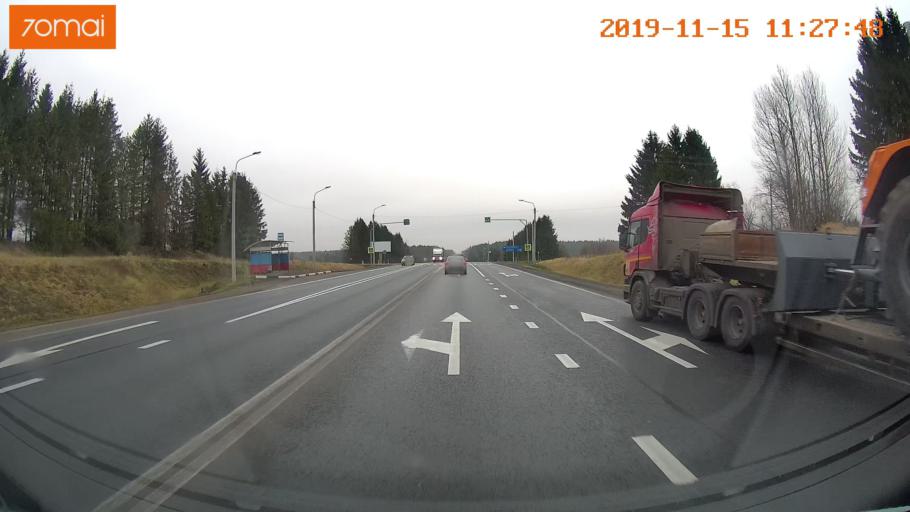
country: RU
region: Vologda
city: Molochnoye
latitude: 59.1706
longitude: 39.4735
